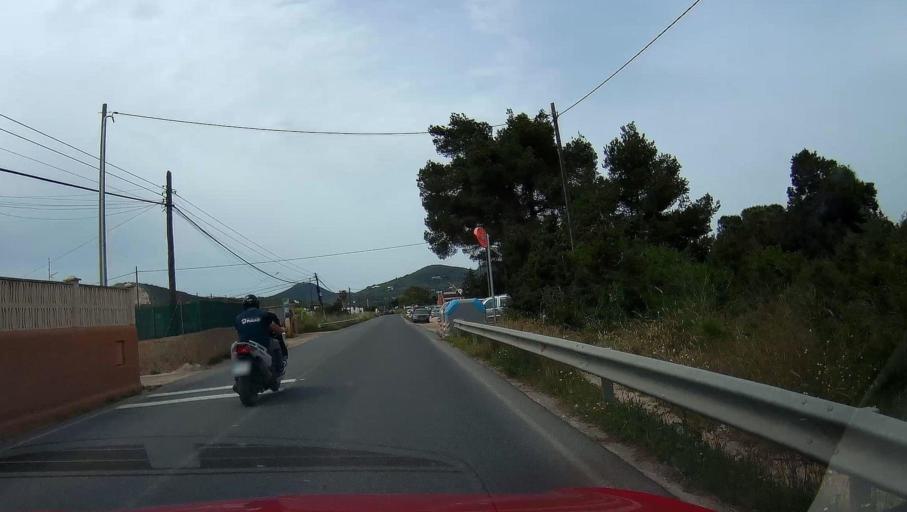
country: ES
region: Balearic Islands
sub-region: Illes Balears
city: Ibiza
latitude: 38.8775
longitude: 1.3642
